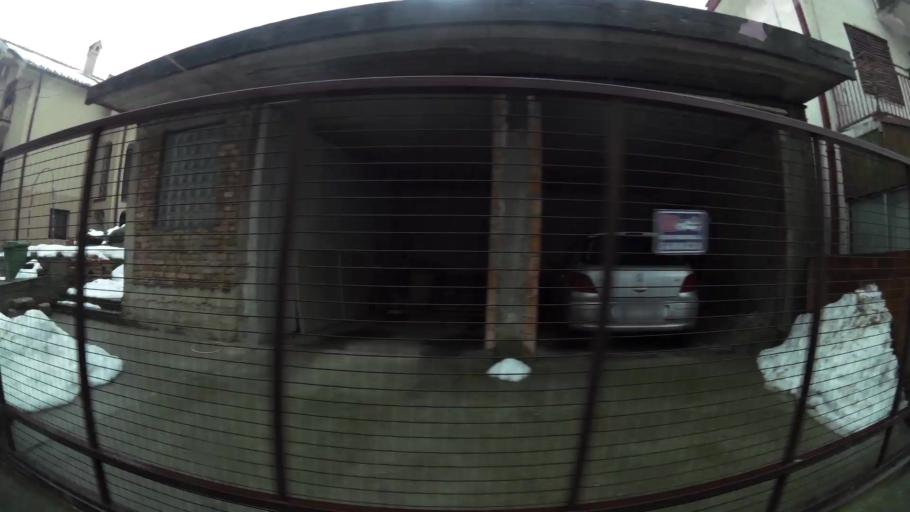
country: RS
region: Central Serbia
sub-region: Belgrade
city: Zvezdara
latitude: 44.7813
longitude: 20.5158
